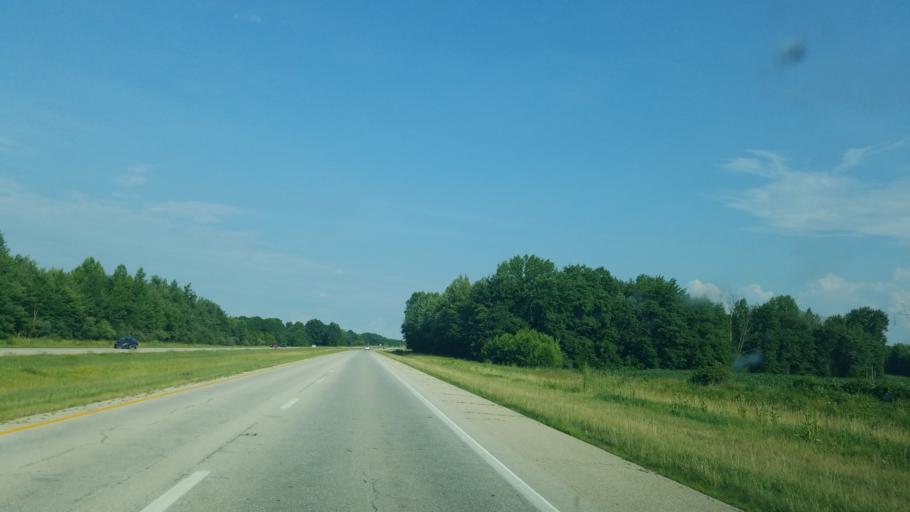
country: US
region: Ohio
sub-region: Brown County
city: Mount Orab
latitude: 39.0308
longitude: -83.8891
